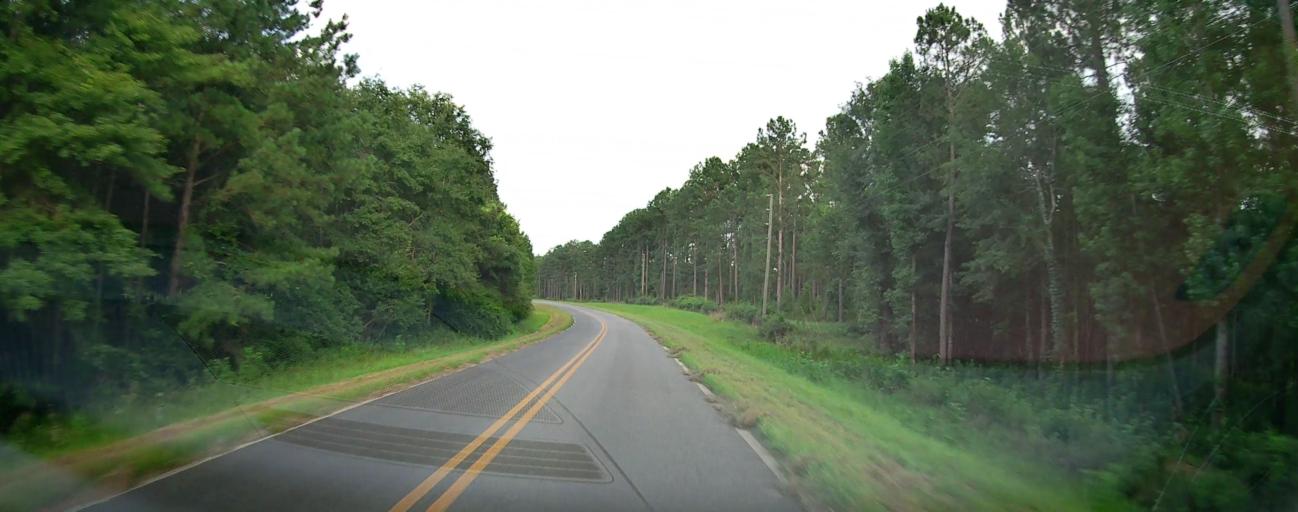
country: US
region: Georgia
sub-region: Crawford County
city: Roberta
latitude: 32.6591
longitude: -84.0618
